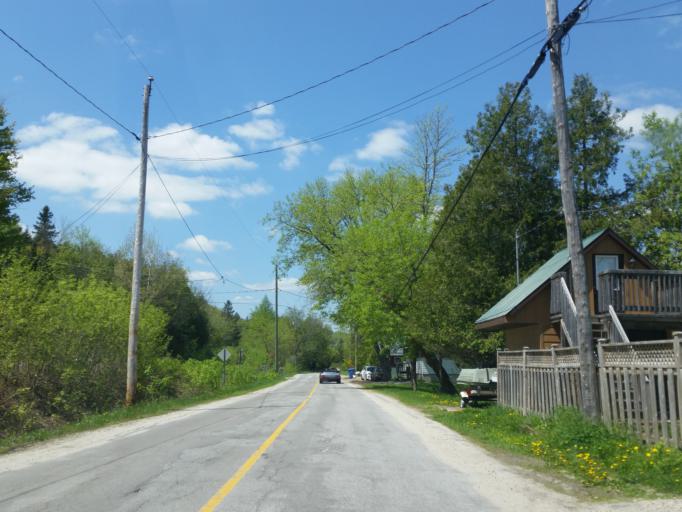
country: CA
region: Quebec
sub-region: Outaouais
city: Wakefield
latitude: 45.6315
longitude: -75.9197
